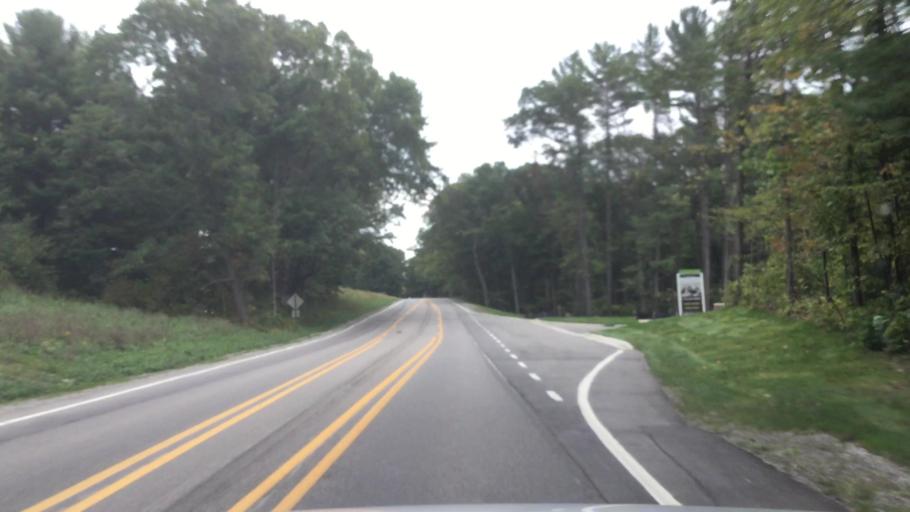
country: US
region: Michigan
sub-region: Livingston County
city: Whitmore Lake
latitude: 42.4619
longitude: -83.7827
